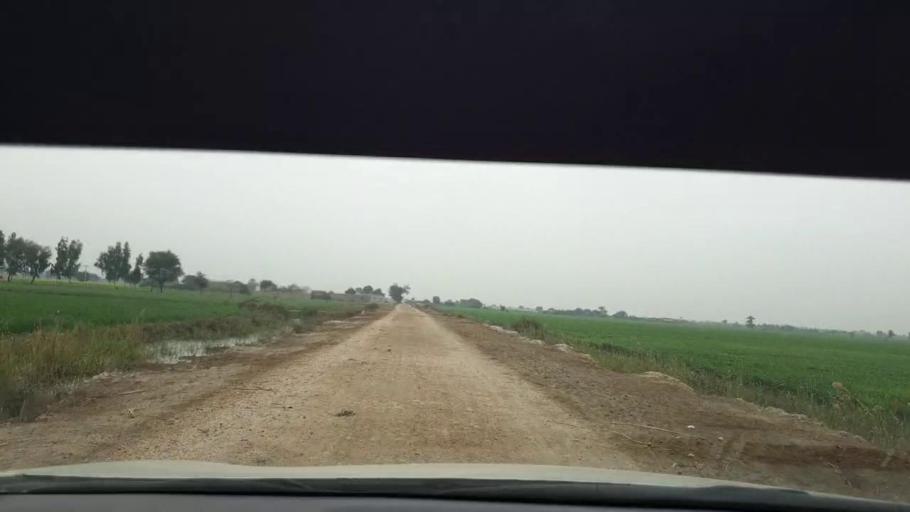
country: PK
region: Sindh
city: Berani
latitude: 25.7590
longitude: 68.8528
